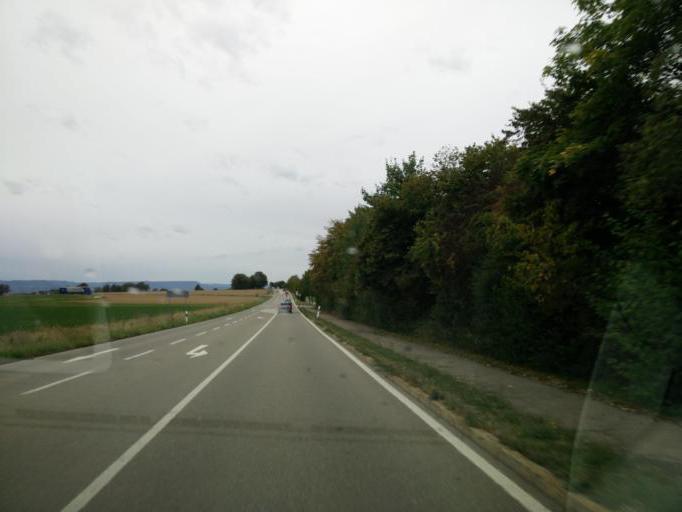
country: DE
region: Baden-Wuerttemberg
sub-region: Tuebingen Region
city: Kusterdingen
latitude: 48.5560
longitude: 9.0973
